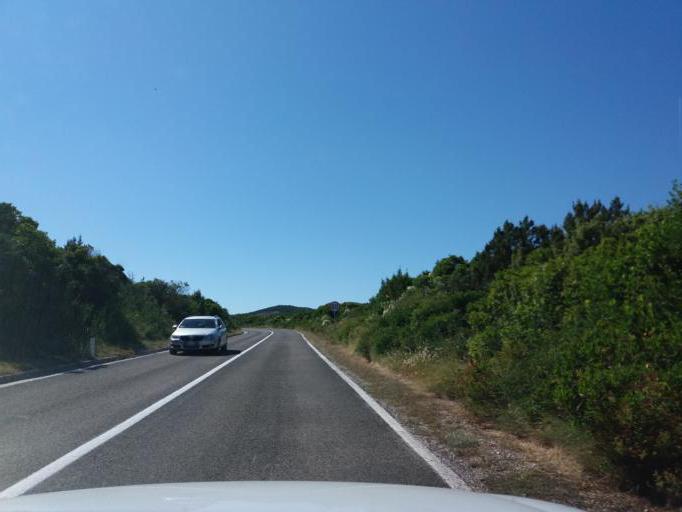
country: HR
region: Zadarska
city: Ugljan
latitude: 44.0795
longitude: 14.9831
